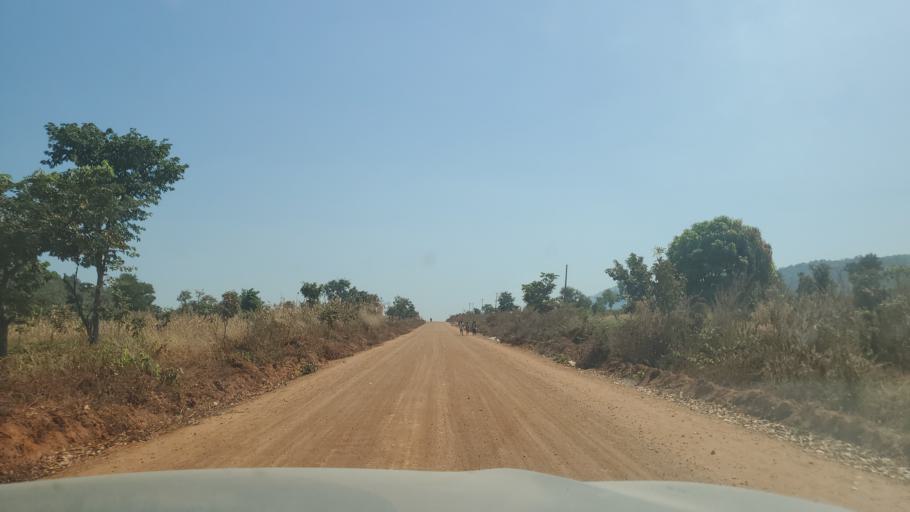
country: NG
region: Niger
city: Gawu Babangida
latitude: 9.2271
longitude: 6.8381
